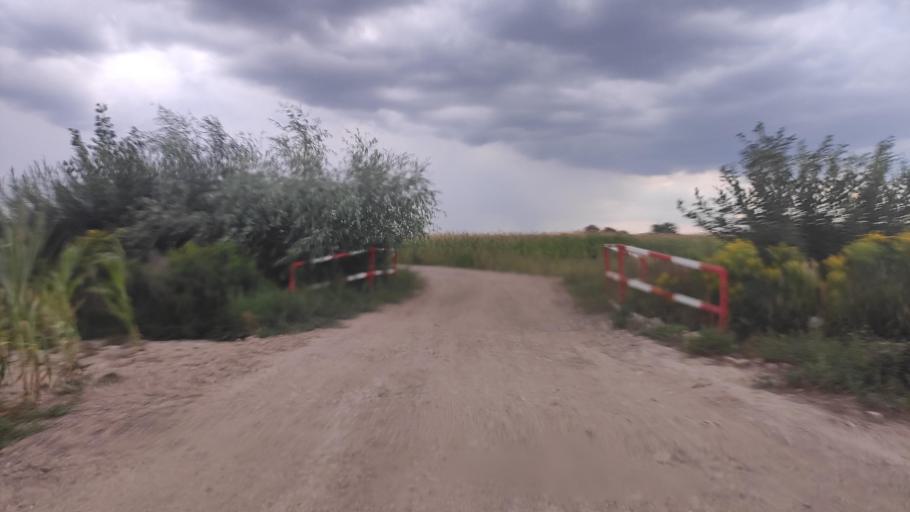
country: PL
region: Greater Poland Voivodeship
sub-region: Powiat poznanski
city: Swarzedz
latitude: 52.3952
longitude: 17.1225
